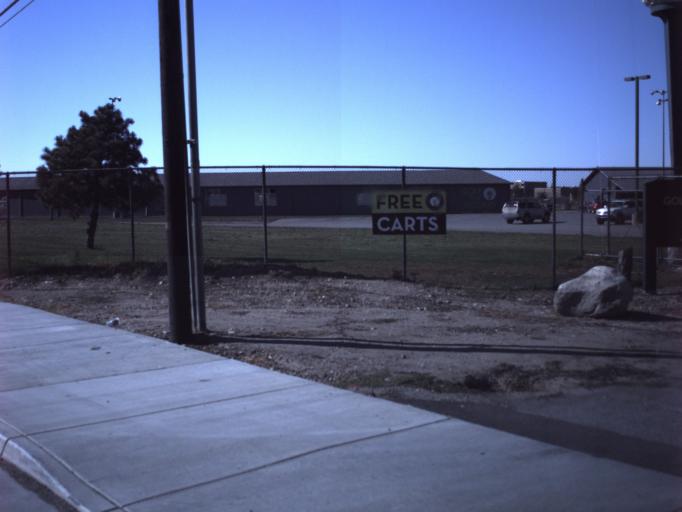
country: US
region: Utah
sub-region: Salt Lake County
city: Centerfield
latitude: 40.6999
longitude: -111.9073
